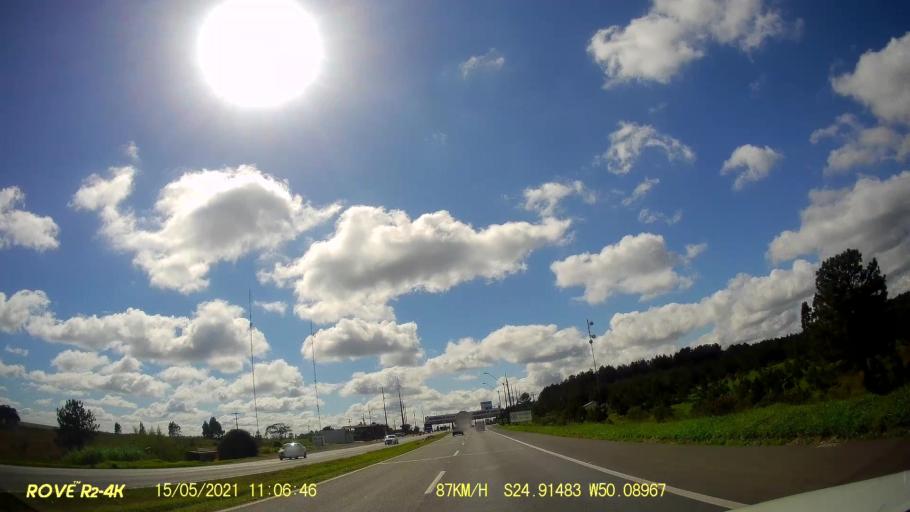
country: BR
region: Parana
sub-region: Carambei
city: Carambei
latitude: -24.9150
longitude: -50.0898
